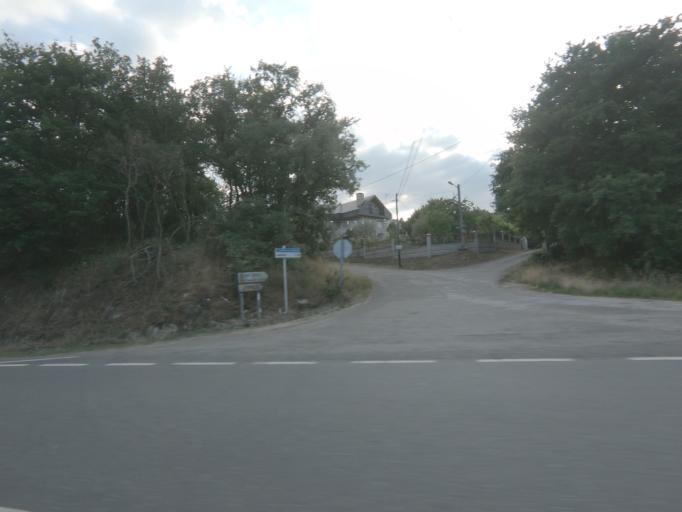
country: ES
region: Galicia
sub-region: Provincia de Ourense
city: Taboadela
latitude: 42.2533
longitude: -7.8354
